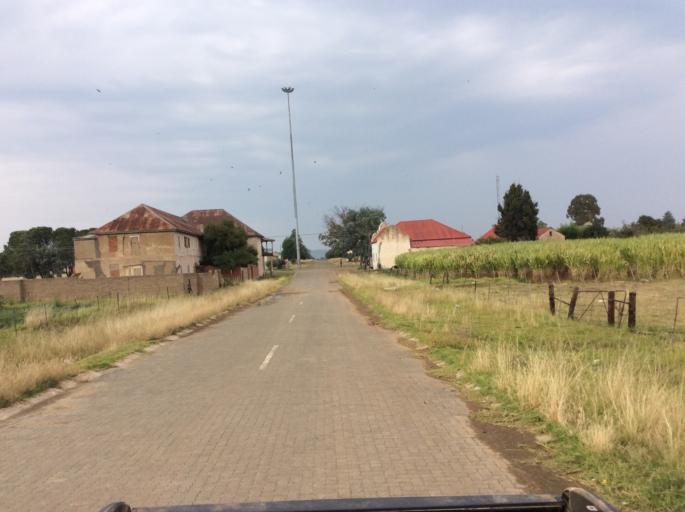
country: LS
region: Mafeteng
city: Mafeteng
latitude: -29.9867
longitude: 27.0138
